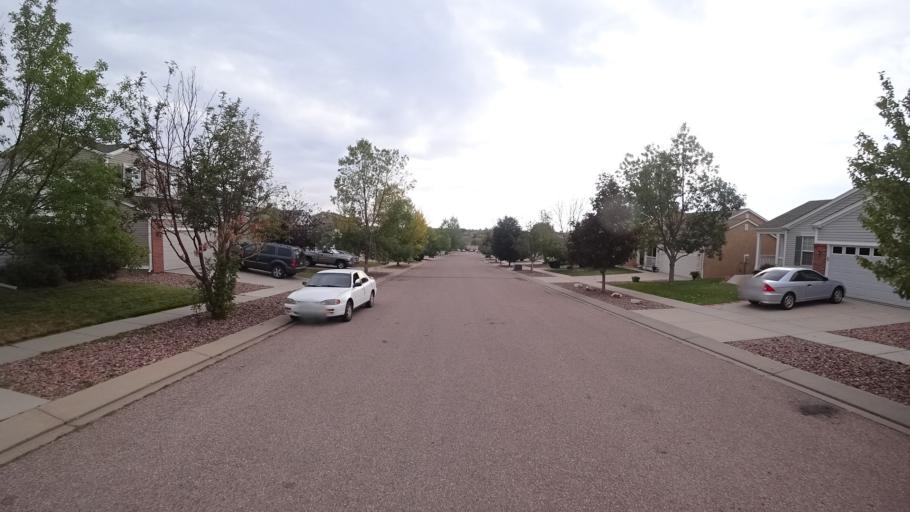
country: US
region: Colorado
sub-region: El Paso County
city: Cimarron Hills
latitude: 38.9172
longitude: -104.7044
